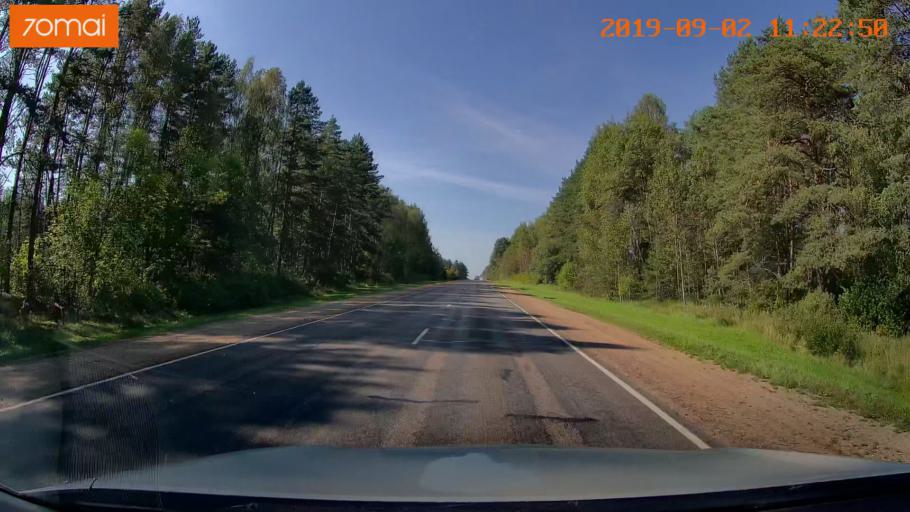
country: RU
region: Smolensk
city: Roslavl'
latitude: 54.0223
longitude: 33.0047
